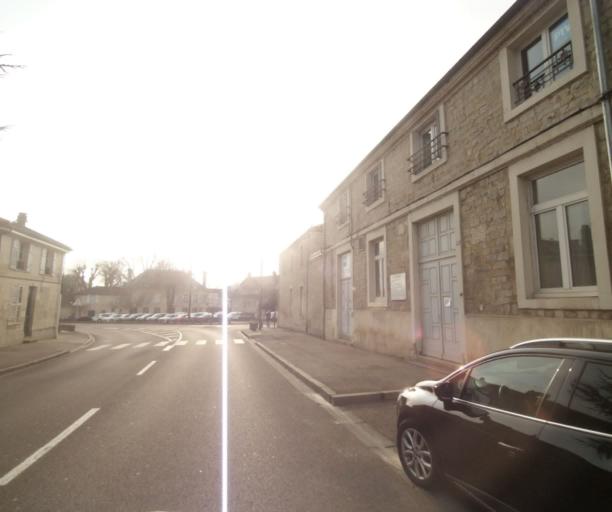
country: FR
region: Champagne-Ardenne
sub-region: Departement de la Haute-Marne
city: Saint-Dizier
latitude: 48.6355
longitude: 4.9483
